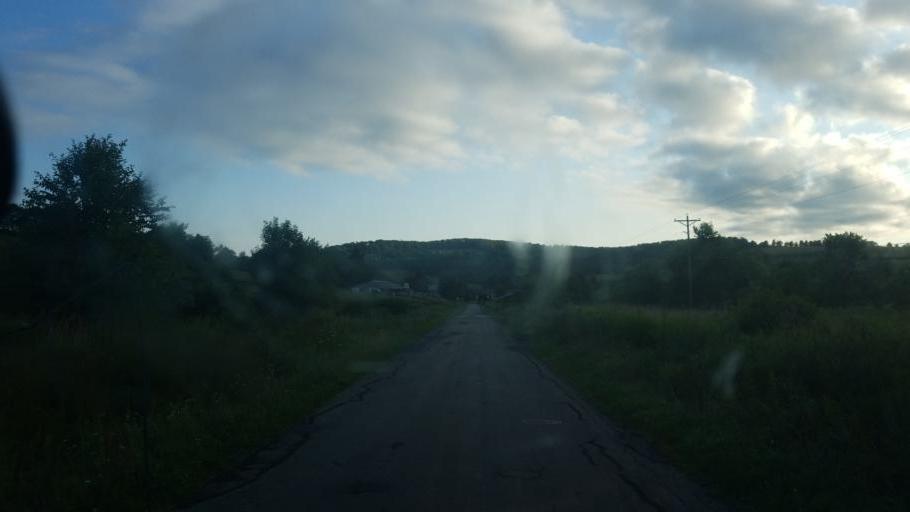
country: US
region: Pennsylvania
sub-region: Potter County
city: Galeton
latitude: 41.8920
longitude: -77.8056
